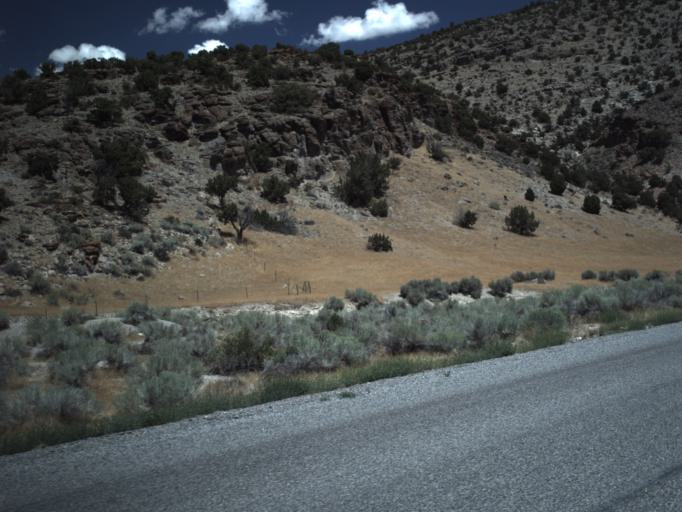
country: US
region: Utah
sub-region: Beaver County
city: Milford
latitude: 39.0834
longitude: -113.6012
